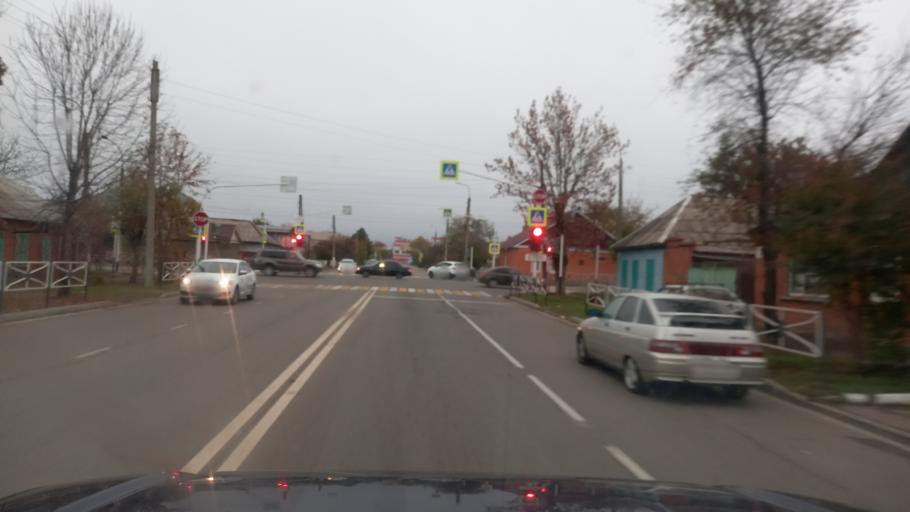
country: RU
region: Adygeya
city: Maykop
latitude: 44.6175
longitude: 40.1023
